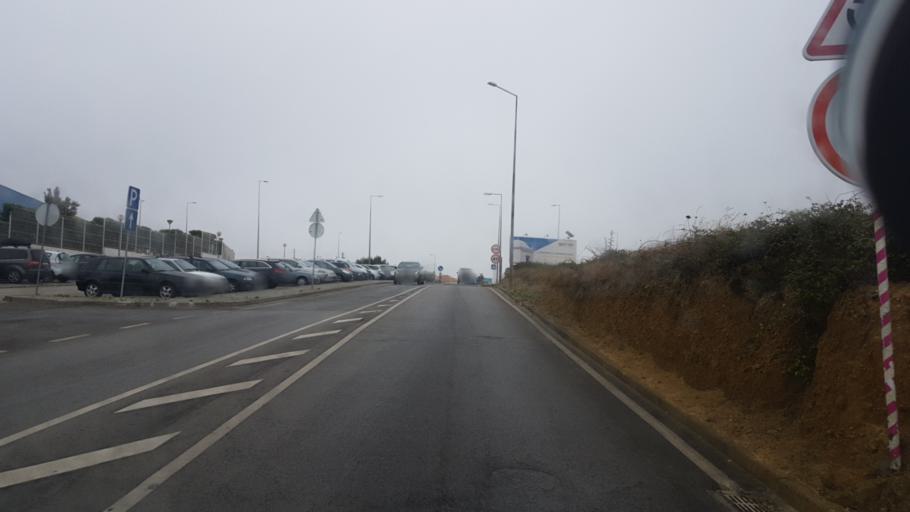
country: PT
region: Lisbon
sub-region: Mafra
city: Ericeira
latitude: 38.9652
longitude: -9.4074
